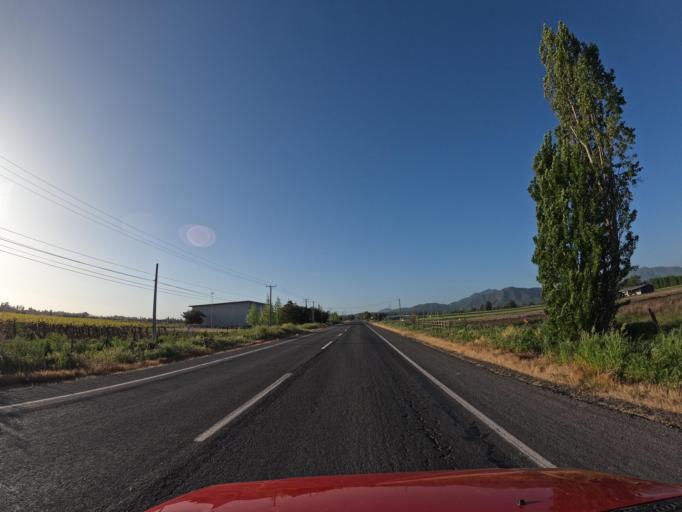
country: CL
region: O'Higgins
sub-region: Provincia de Colchagua
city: Santa Cruz
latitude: -34.4570
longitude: -71.3645
